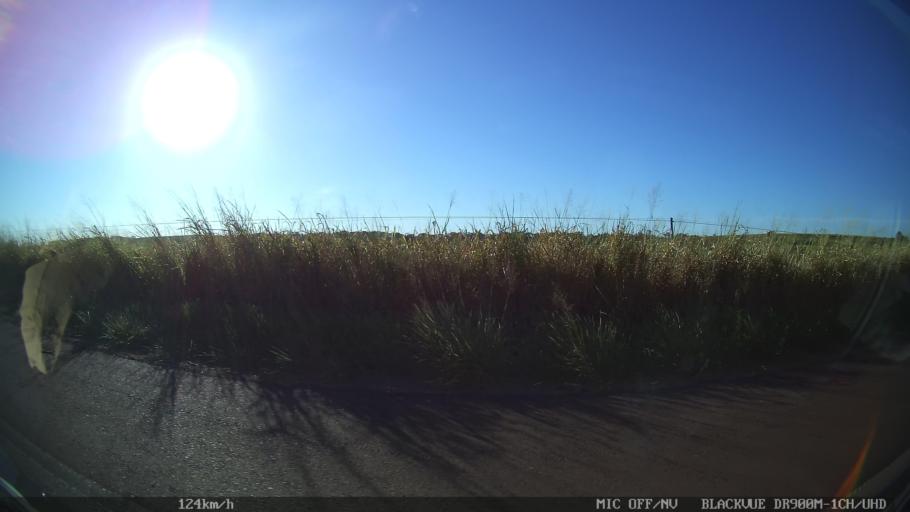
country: BR
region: Sao Paulo
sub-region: Guapiacu
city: Guapiacu
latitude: -20.7403
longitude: -49.0946
